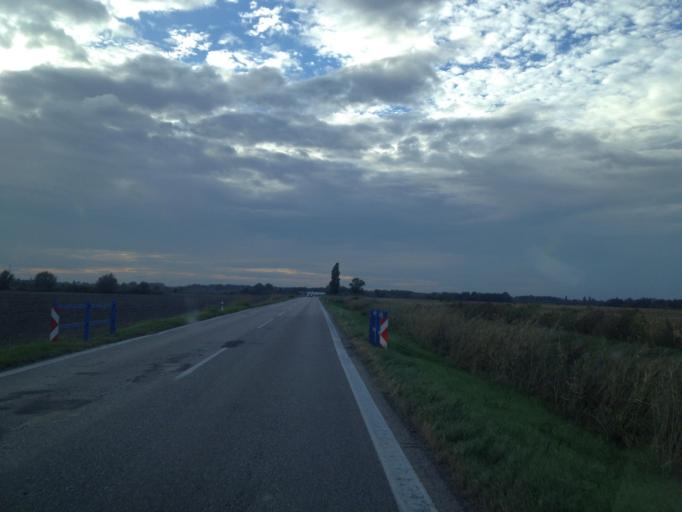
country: SK
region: Nitriansky
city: Komarno
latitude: 47.7628
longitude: 18.1806
